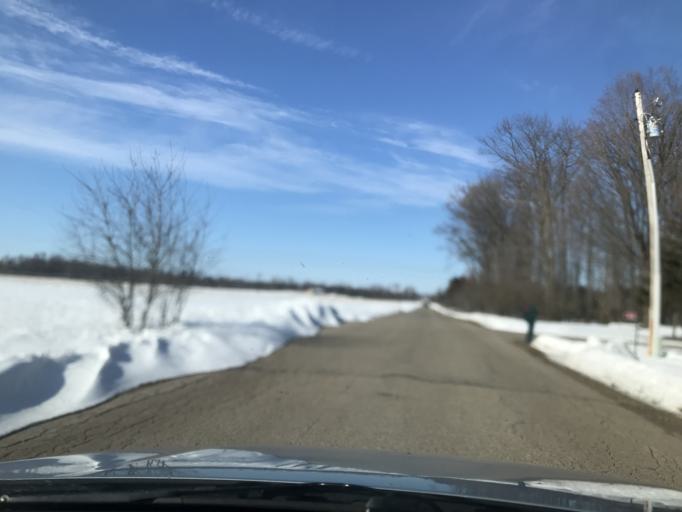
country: US
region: Wisconsin
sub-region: Oconto County
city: Gillett
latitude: 44.9391
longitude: -88.2272
